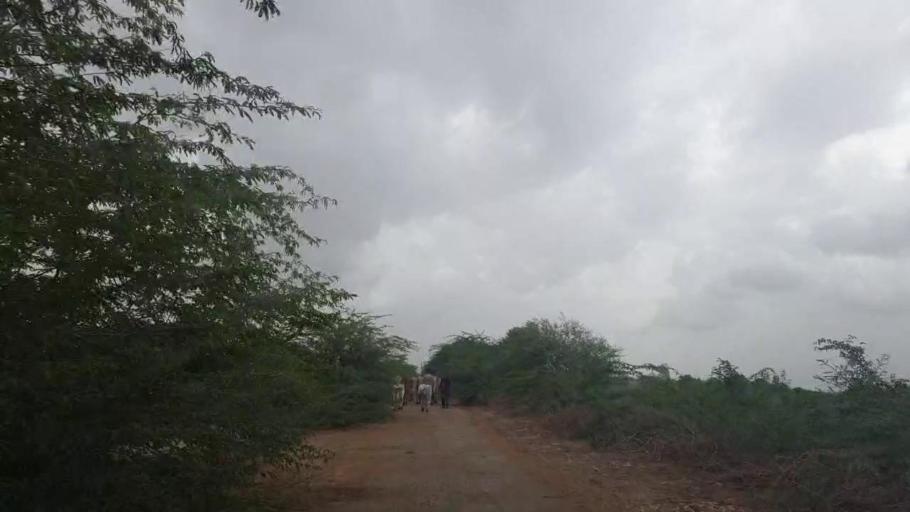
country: PK
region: Sindh
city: Naukot
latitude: 24.8712
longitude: 69.2320
